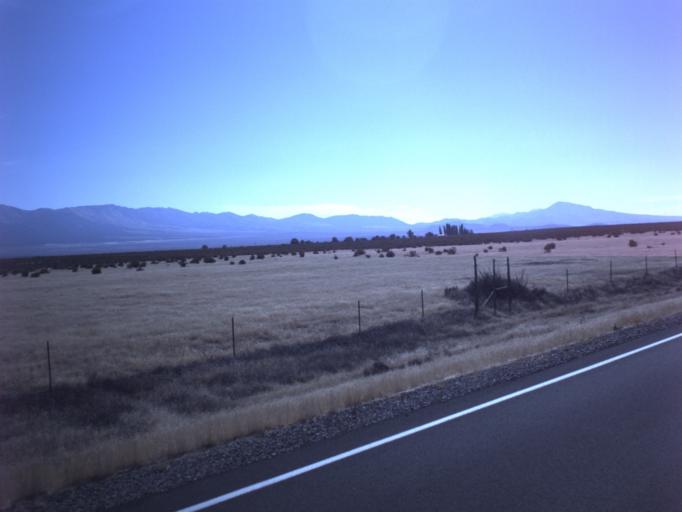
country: US
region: Utah
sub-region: Tooele County
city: Grantsville
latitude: 40.3139
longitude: -112.7435
